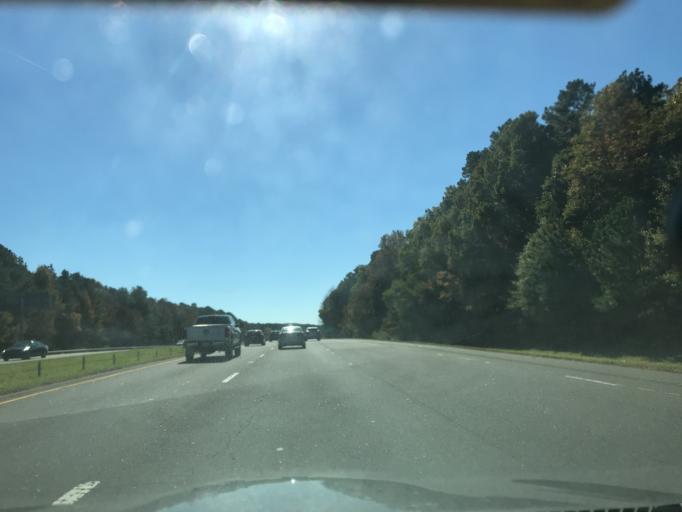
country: US
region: North Carolina
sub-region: Durham County
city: Durham
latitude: 35.9198
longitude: -78.8617
